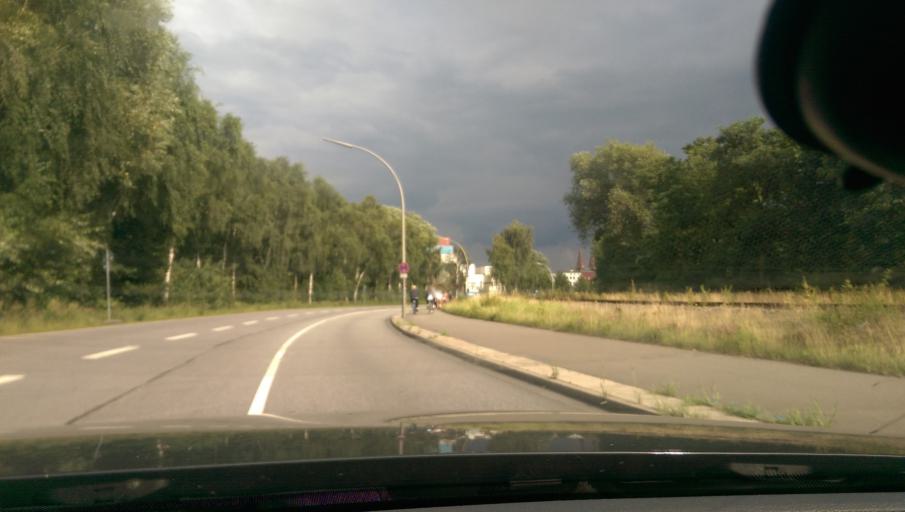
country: DE
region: Hamburg
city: Kleiner Grasbrook
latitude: 53.5065
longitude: 9.9804
